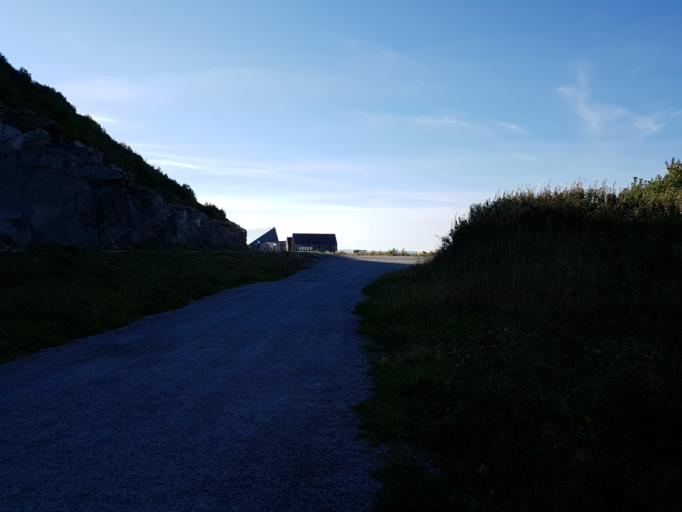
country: NO
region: Sor-Trondelag
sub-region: Afjord
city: A i Afjord
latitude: 64.0482
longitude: 9.9452
